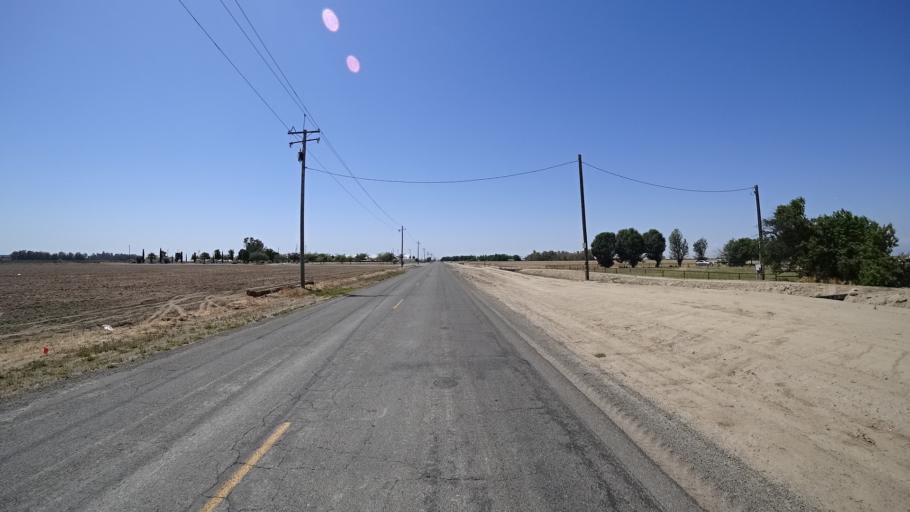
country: US
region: California
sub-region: Kings County
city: Lemoore
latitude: 36.2522
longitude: -119.7988
